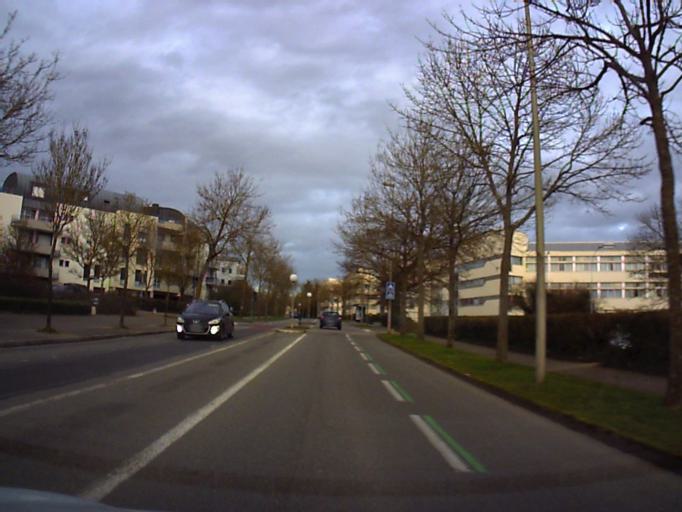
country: FR
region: Brittany
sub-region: Departement d'Ille-et-Vilaine
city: Rennes
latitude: 48.1233
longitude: -1.6463
